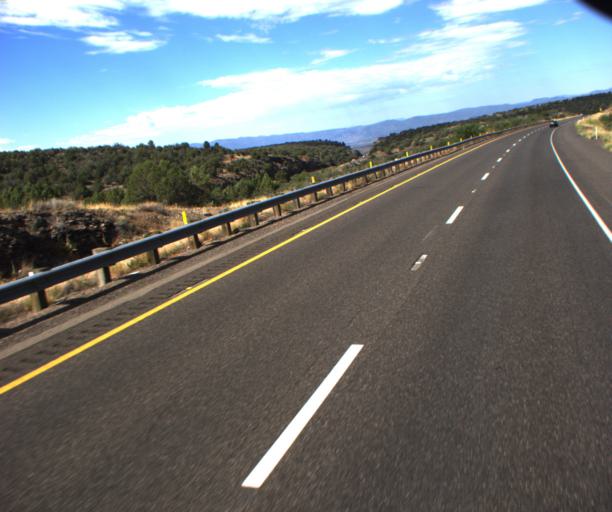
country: US
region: Arizona
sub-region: Yavapai County
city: Big Park
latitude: 34.7241
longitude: -111.7149
